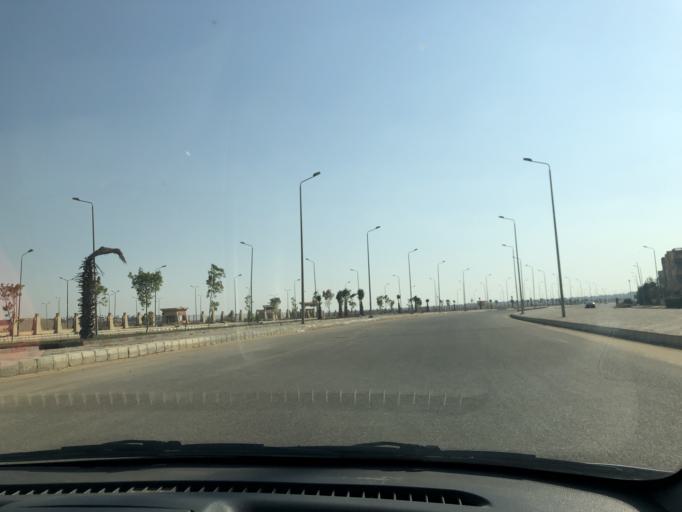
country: EG
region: Al Jizah
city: Madinat Sittah Uktubar
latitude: 29.9294
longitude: 31.0684
